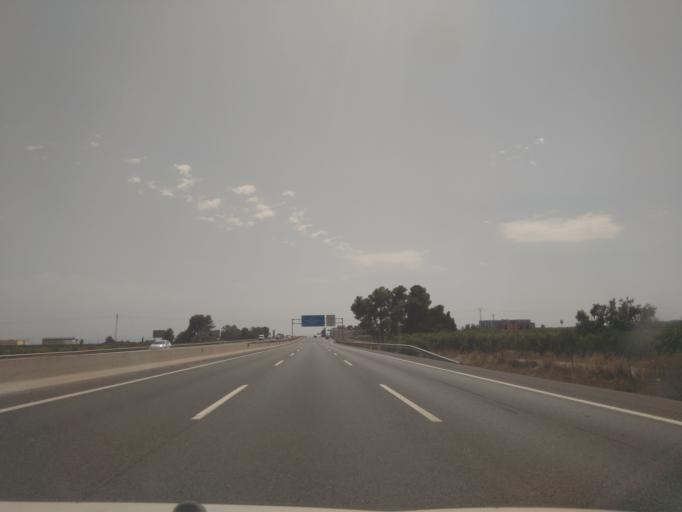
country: ES
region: Valencia
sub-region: Provincia de Valencia
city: Benifaio
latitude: 39.2921
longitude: -0.4530
